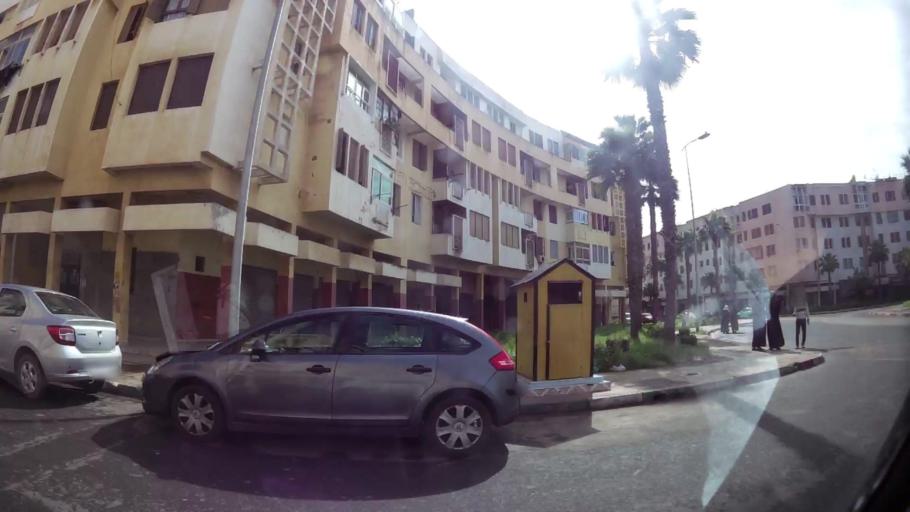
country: MA
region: Grand Casablanca
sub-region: Mohammedia
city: Mohammedia
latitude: 33.6764
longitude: -7.3840
